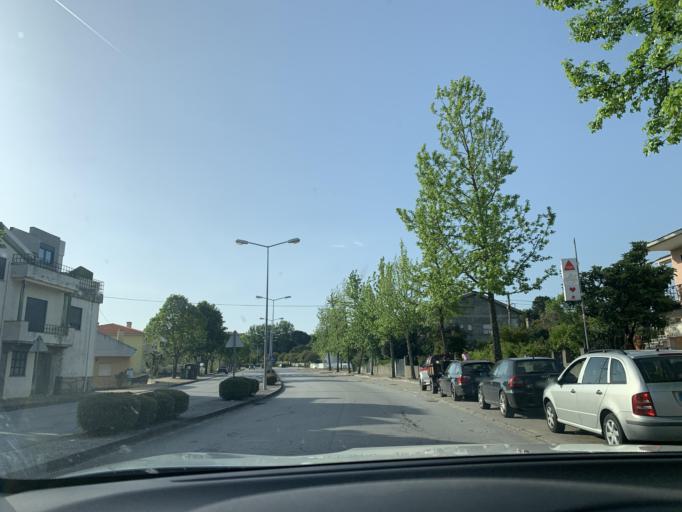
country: PT
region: Viseu
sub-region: Mangualde
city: Mangualde
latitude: 40.5981
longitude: -7.7591
